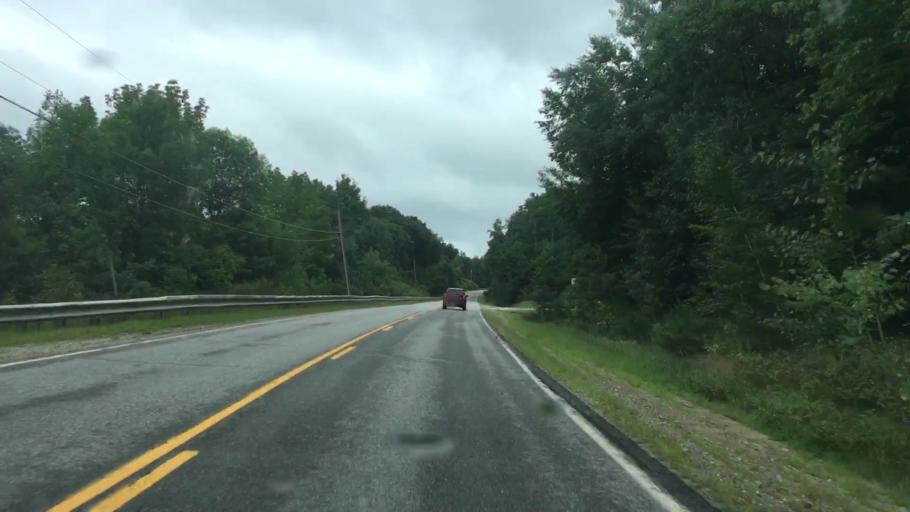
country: US
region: Maine
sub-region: Oxford County
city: Brownfield
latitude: 43.9606
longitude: -70.9018
